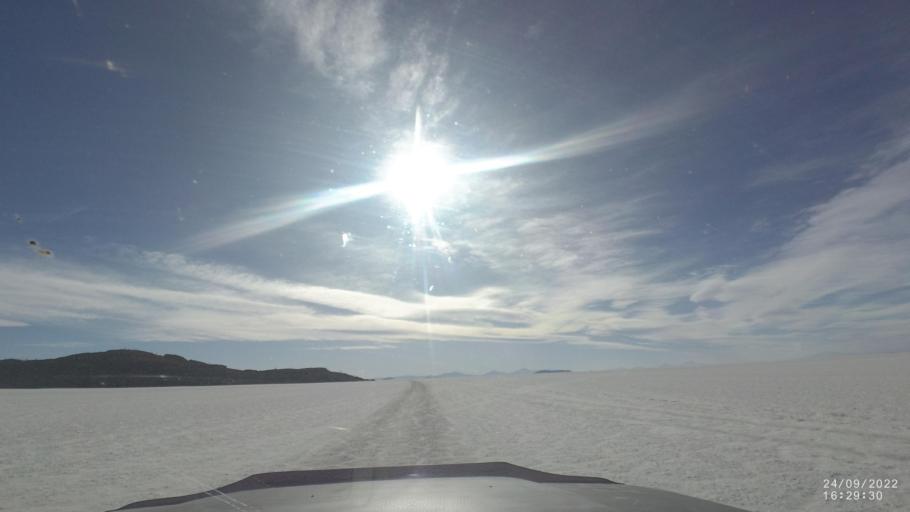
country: BO
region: Potosi
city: Colchani
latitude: -20.2394
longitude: -67.6162
